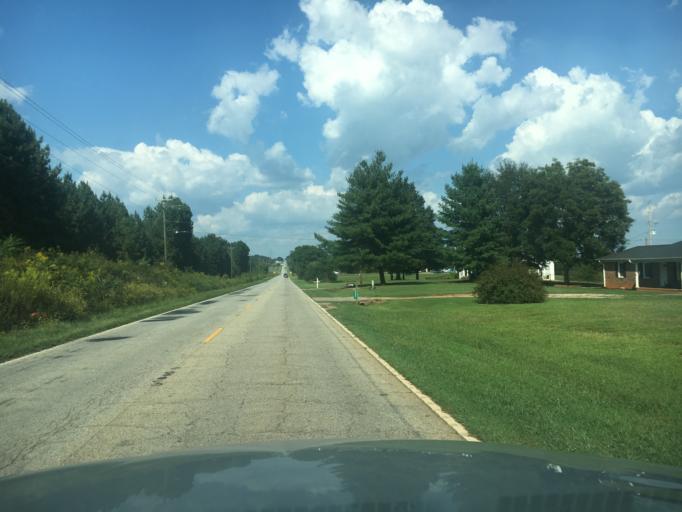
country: US
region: South Carolina
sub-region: Pickens County
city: Liberty
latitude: 34.7331
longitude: -82.6702
